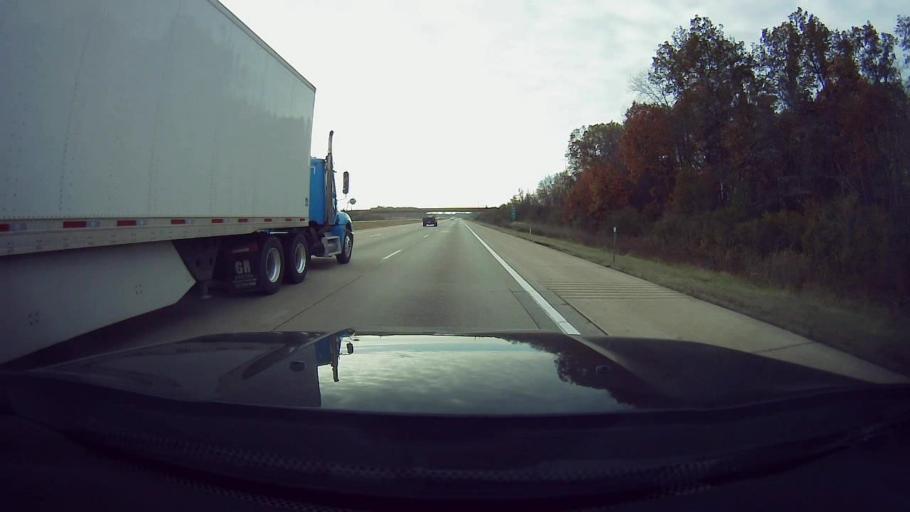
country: US
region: Michigan
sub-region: Monroe County
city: Carleton
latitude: 42.0966
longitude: -83.3778
